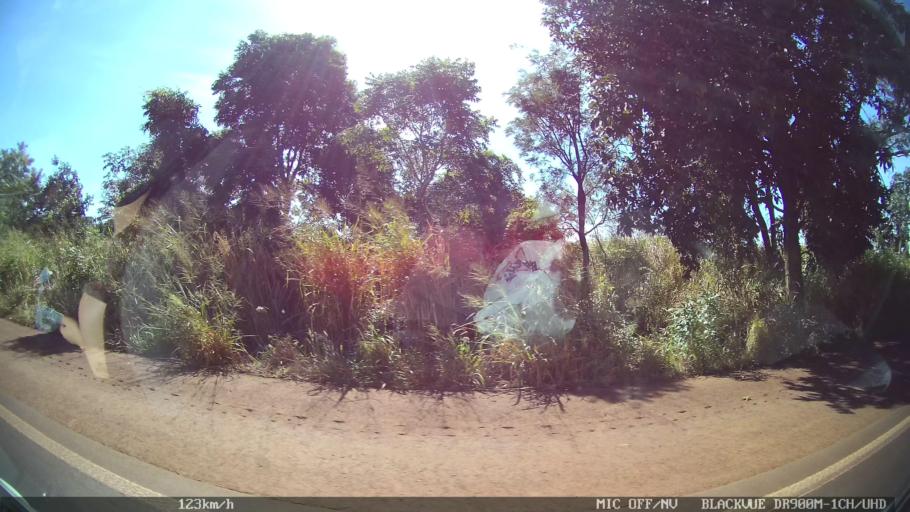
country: BR
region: Sao Paulo
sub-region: Guaira
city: Guaira
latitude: -20.4446
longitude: -48.3748
